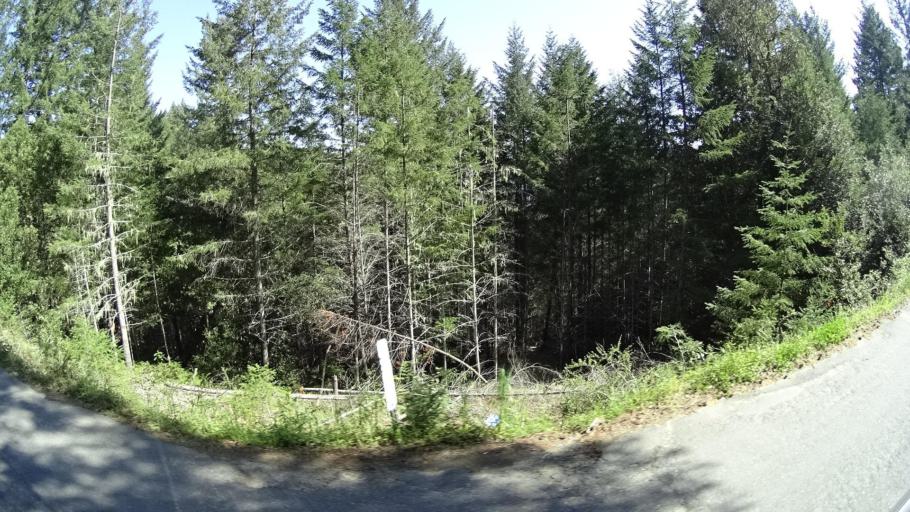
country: US
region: California
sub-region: Humboldt County
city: Redway
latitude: 40.0761
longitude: -123.6529
